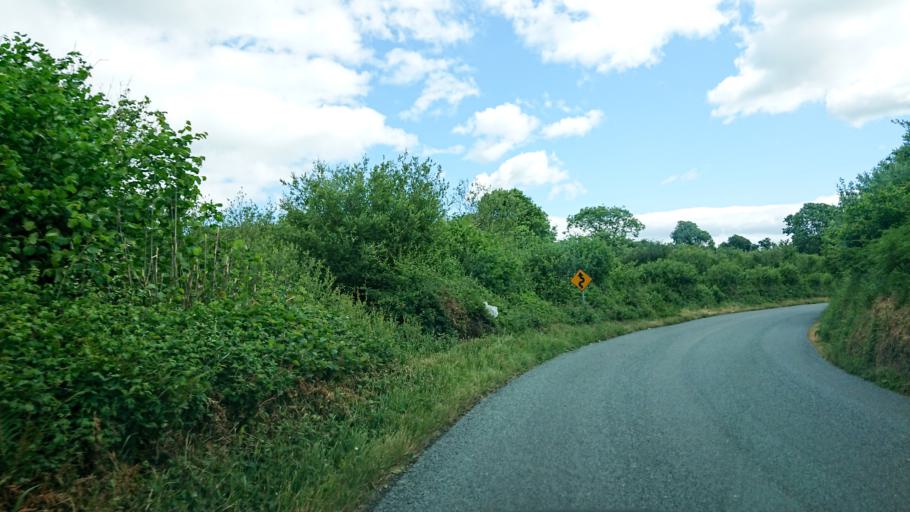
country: IE
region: Munster
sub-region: Waterford
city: Tra Mhor
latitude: 52.1785
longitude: -7.1533
